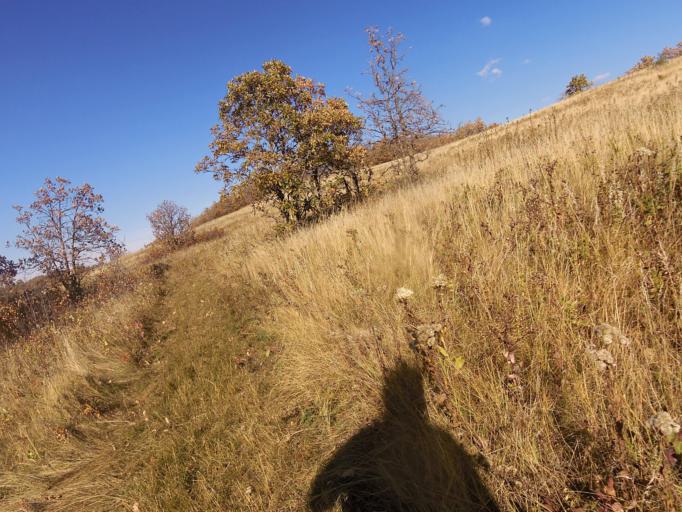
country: CA
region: Manitoba
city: Morden
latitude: 48.9466
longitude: -98.0750
